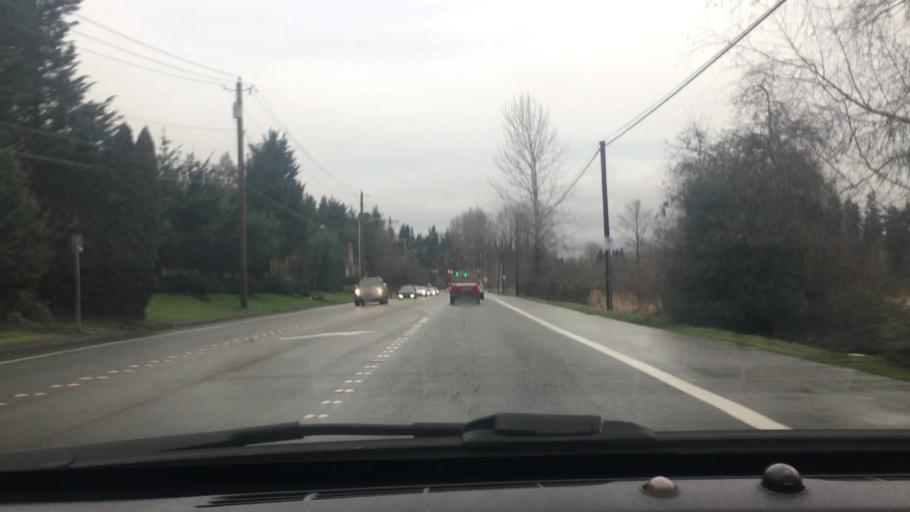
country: US
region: Washington
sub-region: King County
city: Redmond
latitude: 47.6561
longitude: -122.1193
